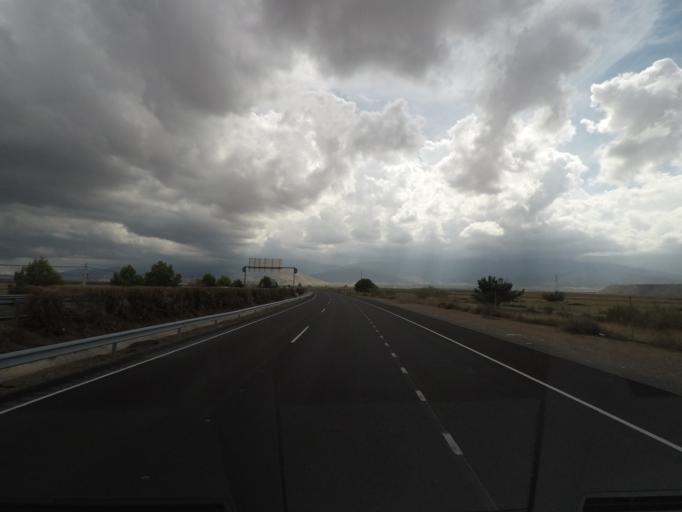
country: ES
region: Andalusia
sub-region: Provincia de Granada
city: Albunan
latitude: 37.2274
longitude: -3.0817
